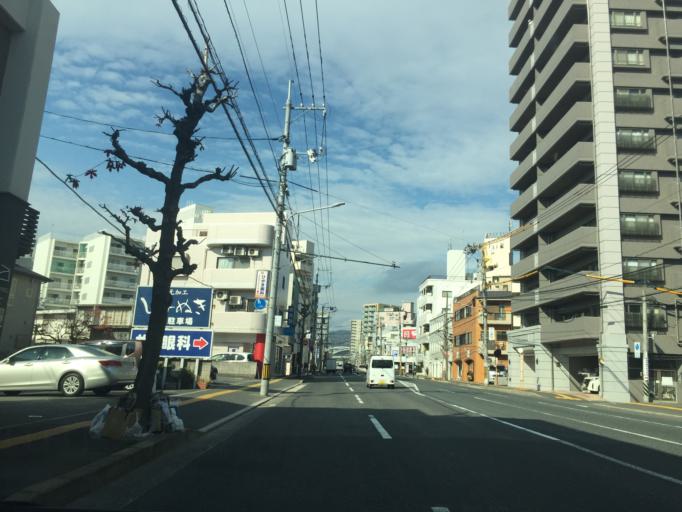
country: JP
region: Hiroshima
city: Hiroshima-shi
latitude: 34.4108
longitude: 132.4708
